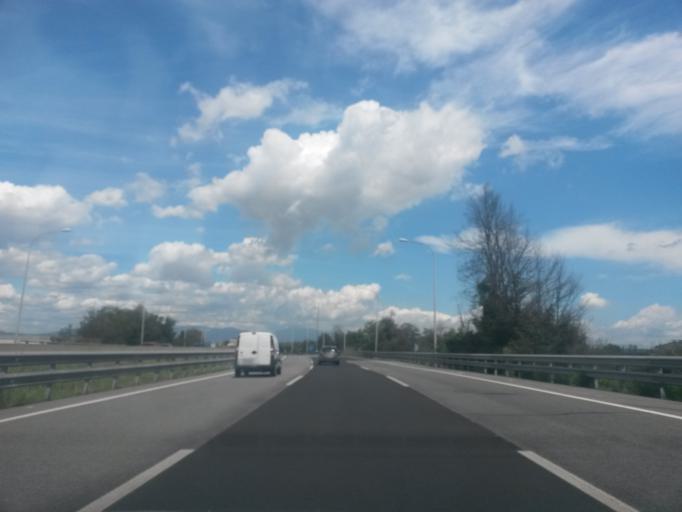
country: ES
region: Catalonia
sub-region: Provincia de Barcelona
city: Montmelo
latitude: 41.5452
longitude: 2.2333
